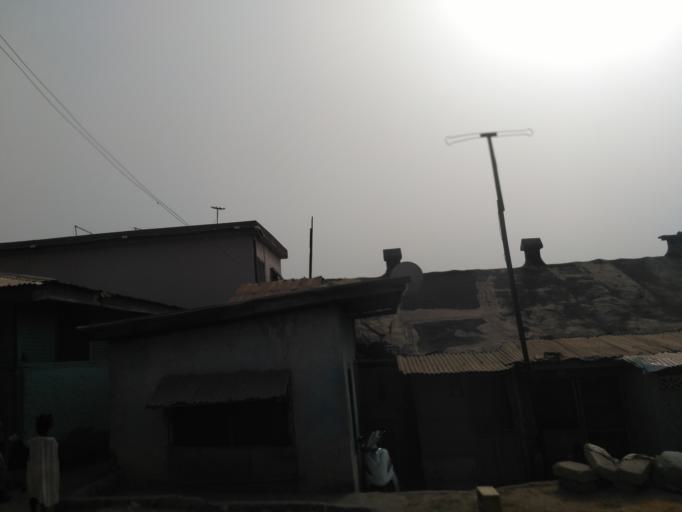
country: GH
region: Ashanti
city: Kumasi
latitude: 6.7013
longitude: -1.6047
